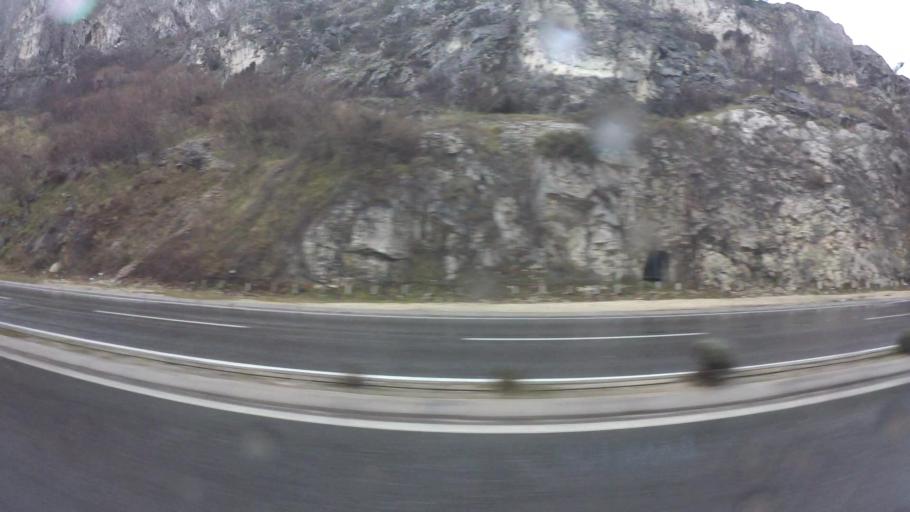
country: BA
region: Federation of Bosnia and Herzegovina
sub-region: Hercegovacko-Bosanski Kanton
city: Mostar
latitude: 43.3307
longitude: 17.8153
